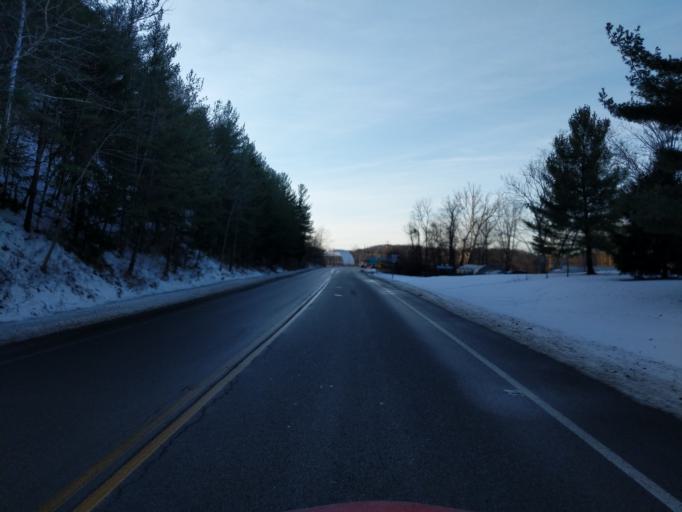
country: US
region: Ohio
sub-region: Athens County
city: Athens
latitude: 39.3292
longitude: -82.1246
